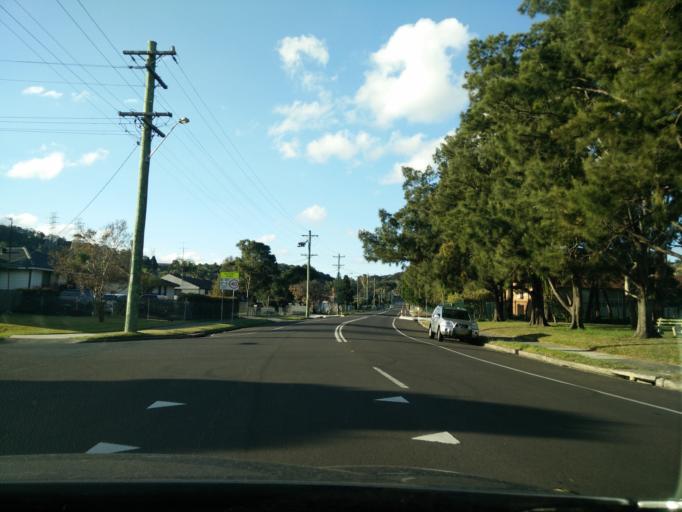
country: AU
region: New South Wales
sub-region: Wollongong
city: Berkeley
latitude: -34.4759
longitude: 150.8396
